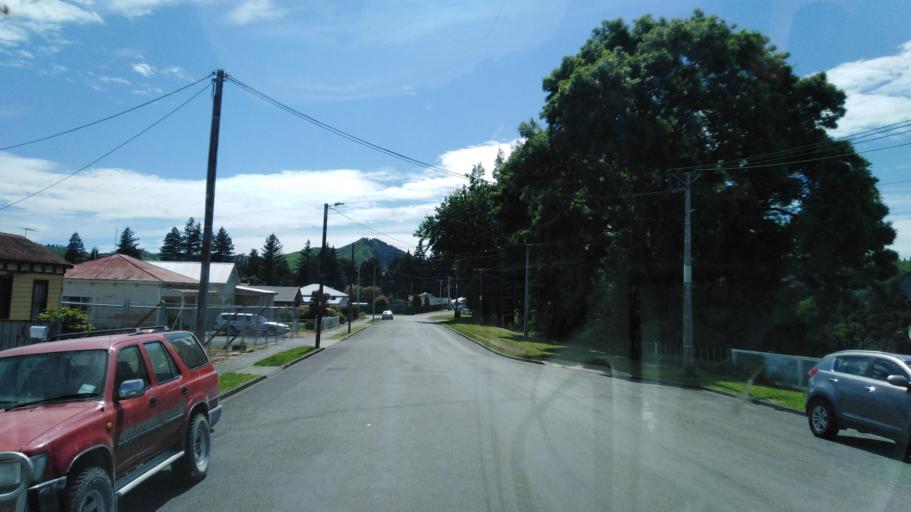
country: NZ
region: Manawatu-Wanganui
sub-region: Ruapehu District
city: Waiouru
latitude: -39.6794
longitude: 175.8011
